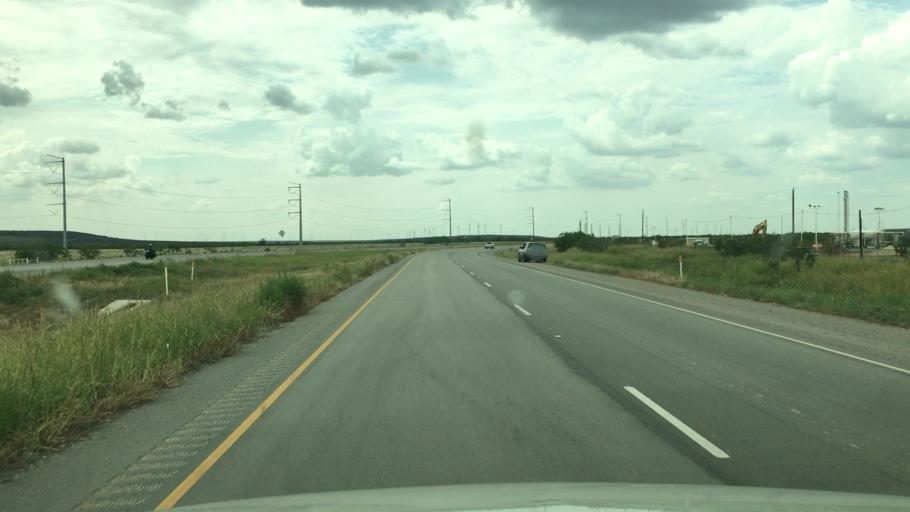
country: US
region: Texas
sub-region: Glasscock County
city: Garden City
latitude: 31.9681
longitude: -101.2368
